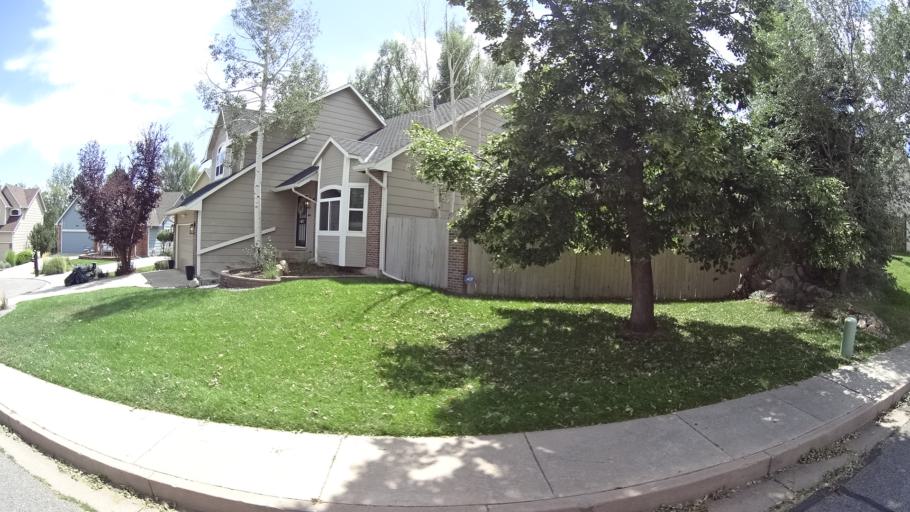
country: US
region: Colorado
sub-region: El Paso County
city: Stratmoor
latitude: 38.7709
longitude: -104.8165
